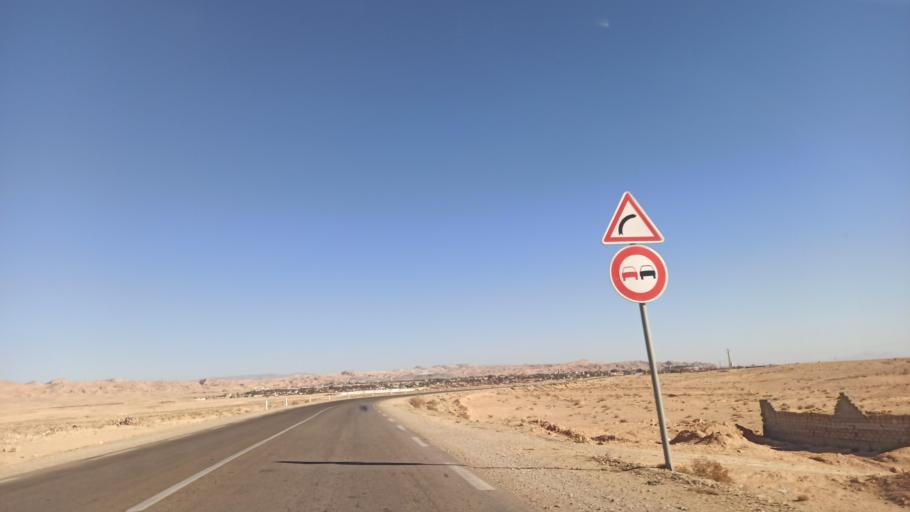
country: TN
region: Gafsa
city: Al Metlaoui
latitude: 34.3047
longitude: 8.3635
